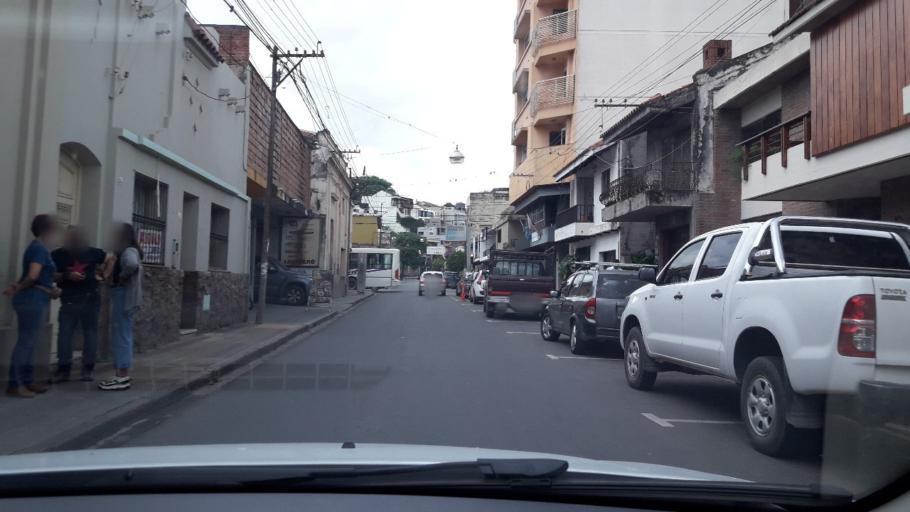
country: AR
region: Jujuy
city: San Salvador de Jujuy
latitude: -24.1857
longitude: -65.3105
